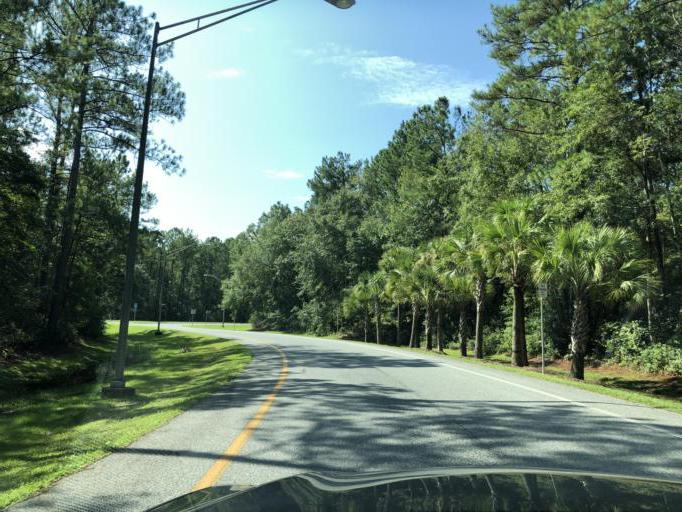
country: US
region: Florida
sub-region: Walton County
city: DeFuniak Springs
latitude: 30.7123
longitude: -85.9331
